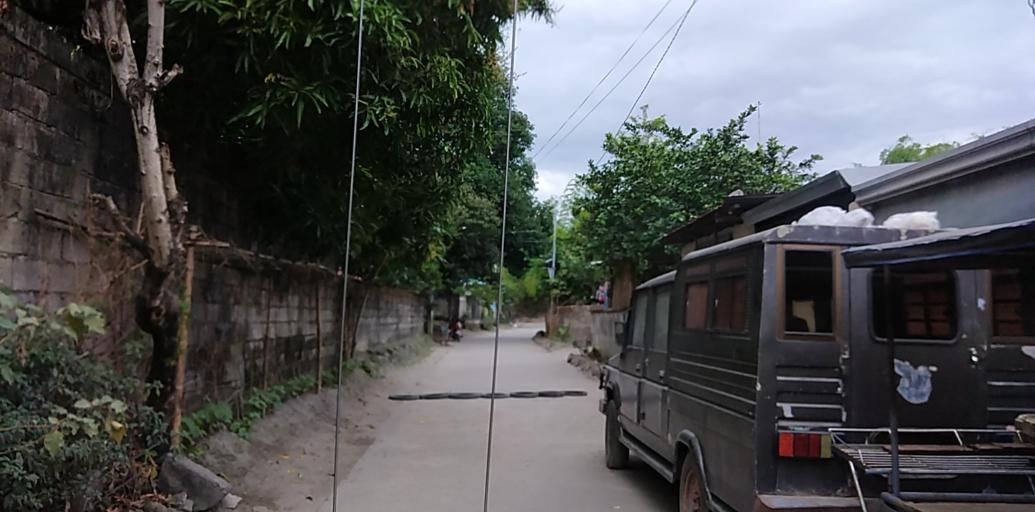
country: PH
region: Central Luzon
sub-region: Province of Pampanga
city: Pulung Santol
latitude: 15.0454
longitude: 120.5618
